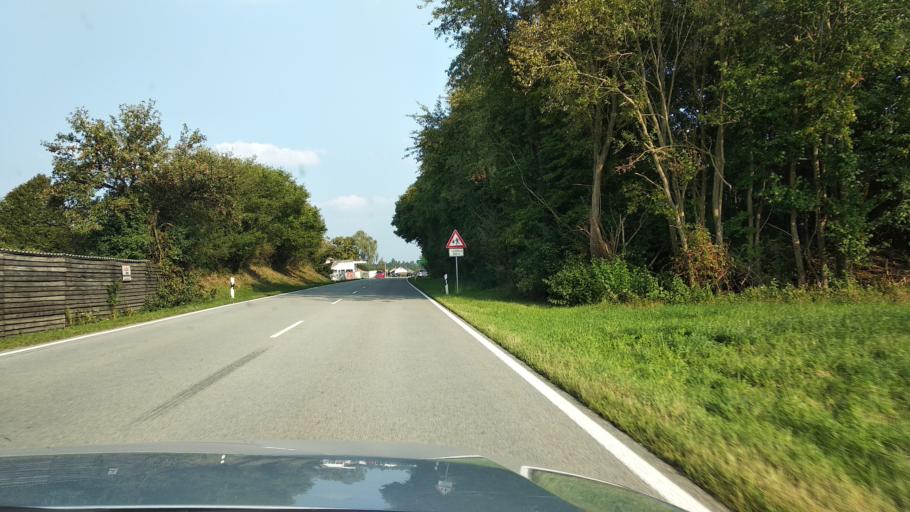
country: DE
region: Bavaria
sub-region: Upper Bavaria
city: Pfaffing
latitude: 48.0774
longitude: 12.1251
